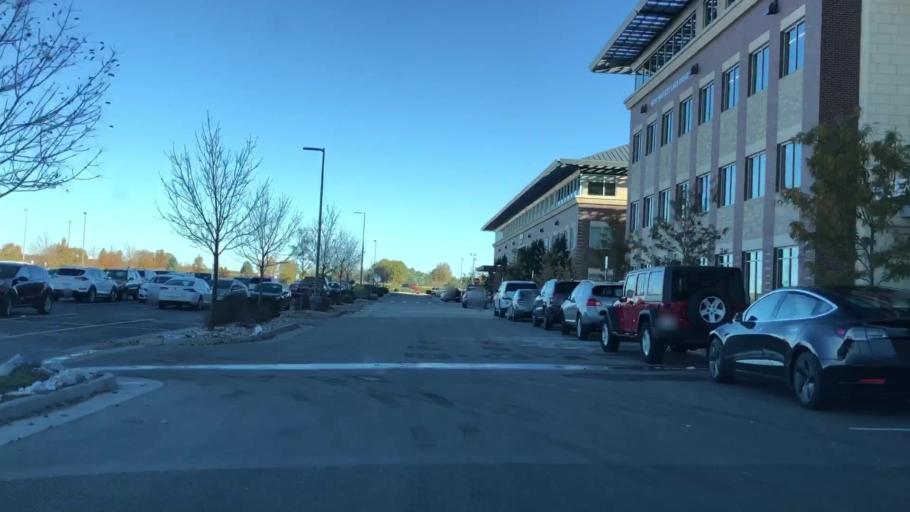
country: US
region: Colorado
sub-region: Larimer County
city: Loveland
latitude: 40.4226
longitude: -105.0041
